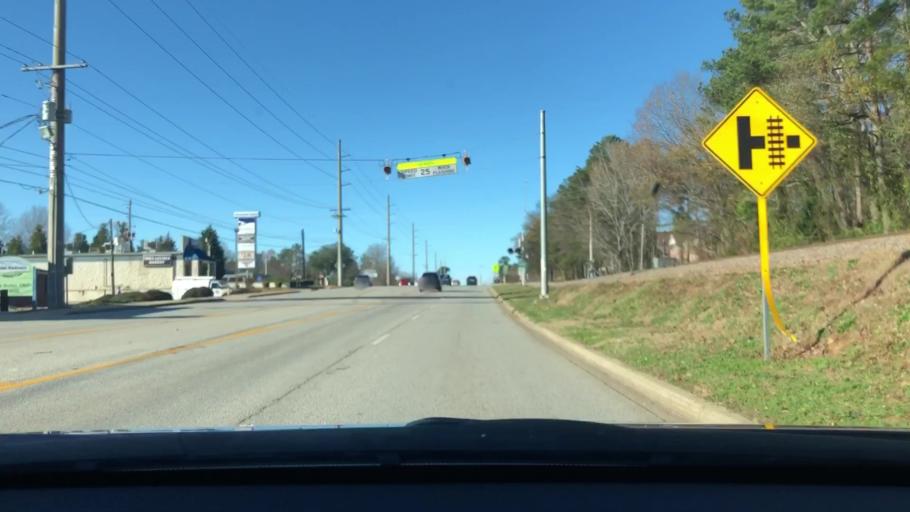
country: US
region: South Carolina
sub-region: Lexington County
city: Irmo
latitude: 34.0719
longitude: -81.1752
